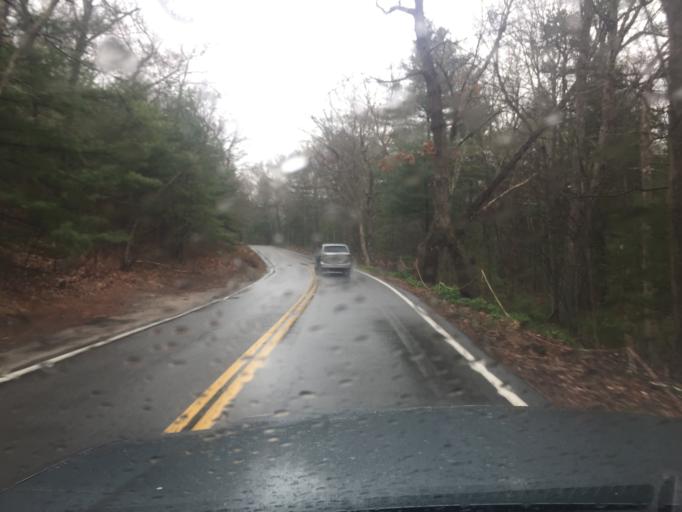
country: US
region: Massachusetts
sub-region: Norfolk County
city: Dover
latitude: 42.2279
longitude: -71.2552
